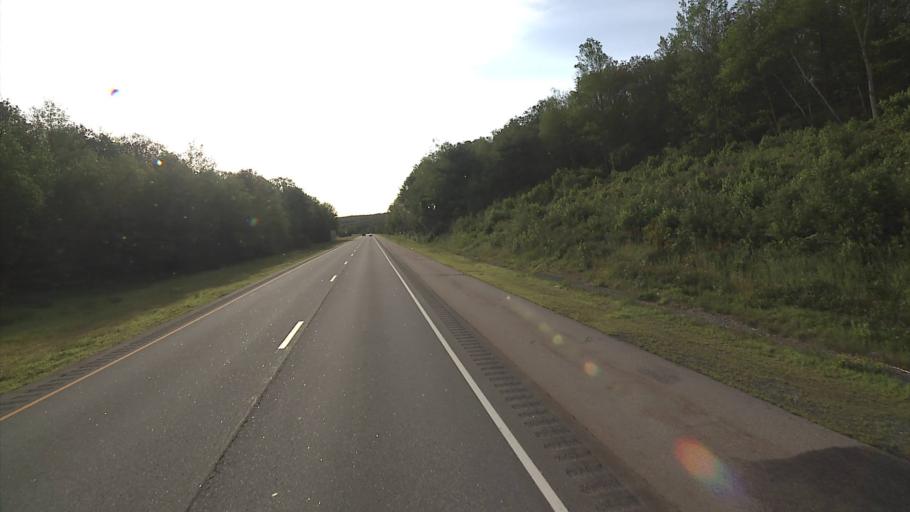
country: US
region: Connecticut
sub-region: New London County
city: Colchester
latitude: 41.5660
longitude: -72.2516
